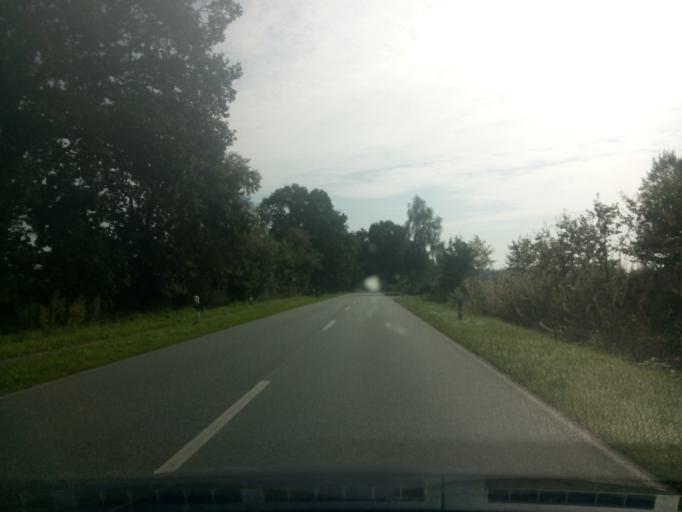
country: DE
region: Lower Saxony
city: Osterholz-Scharmbeck
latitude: 53.2626
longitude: 8.7696
